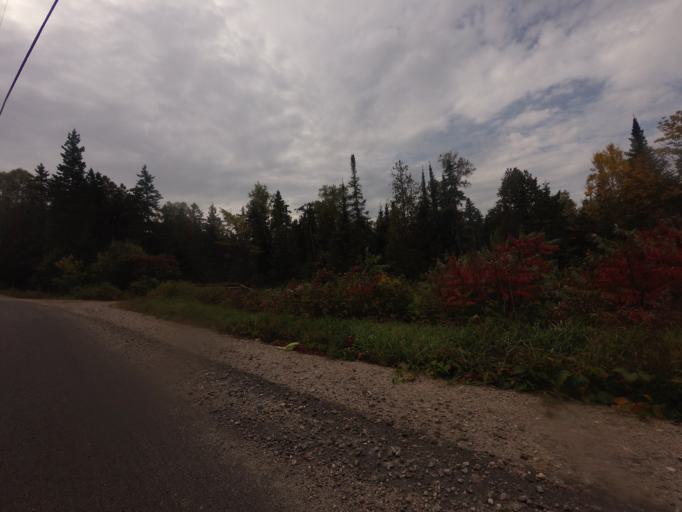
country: CA
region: Quebec
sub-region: Outaouais
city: Wakefield
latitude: 45.9868
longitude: -75.9452
